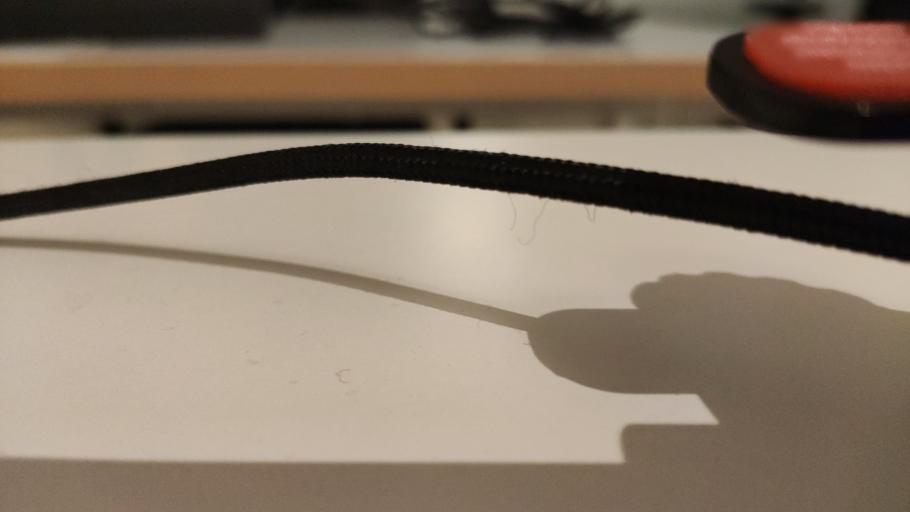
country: RU
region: Moskovskaya
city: Bogorodskoye
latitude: 56.4399
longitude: 37.9065
